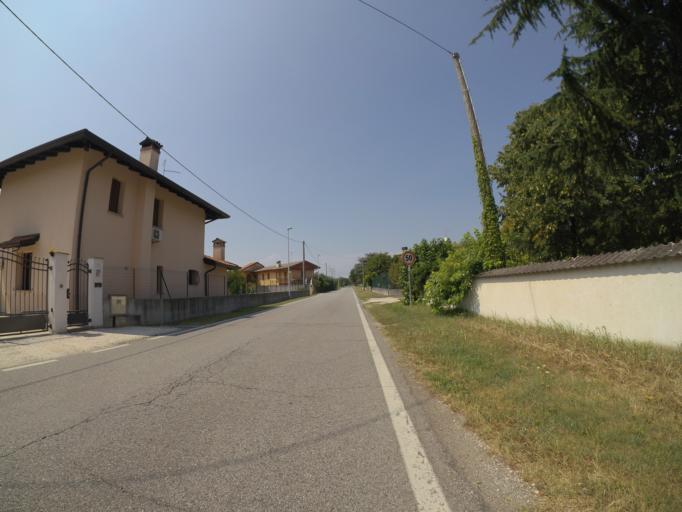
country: IT
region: Friuli Venezia Giulia
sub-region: Provincia di Udine
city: Castions di Strada
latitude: 45.9128
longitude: 13.1725
